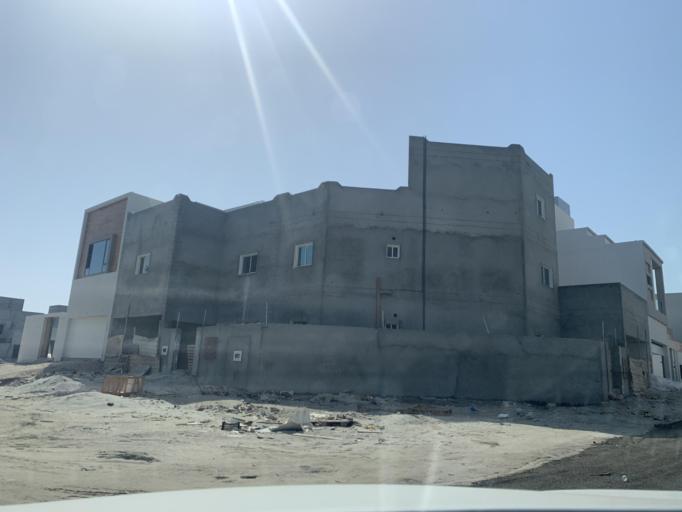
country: BH
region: Manama
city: Jidd Hafs
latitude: 26.2295
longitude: 50.4650
